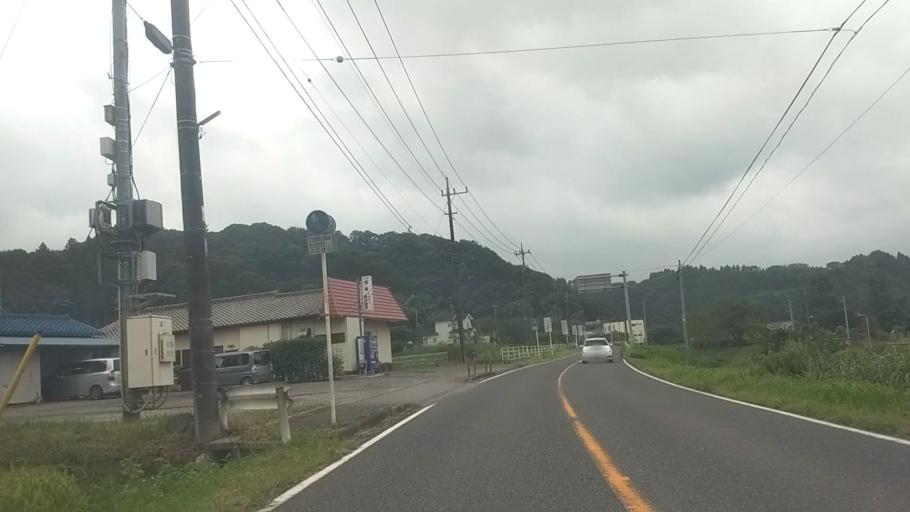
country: JP
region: Chiba
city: Kawaguchi
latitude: 35.2594
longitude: 140.0643
